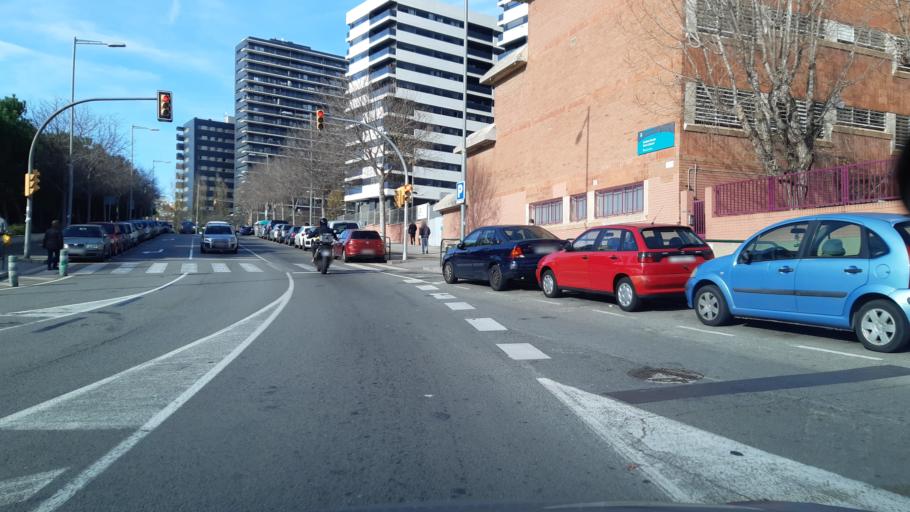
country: ES
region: Catalonia
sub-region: Provincia de Barcelona
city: L'Hospitalet de Llobregat
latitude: 41.3744
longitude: 2.1113
